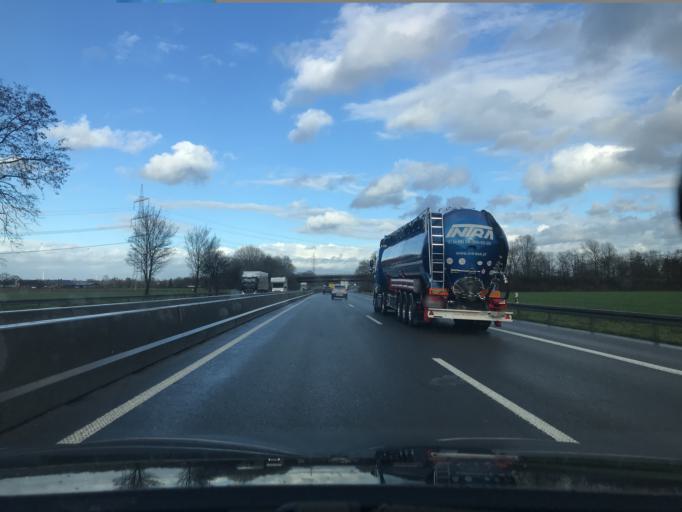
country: DE
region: North Rhine-Westphalia
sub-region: Regierungsbezirk Dusseldorf
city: Moers
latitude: 51.4339
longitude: 6.5868
